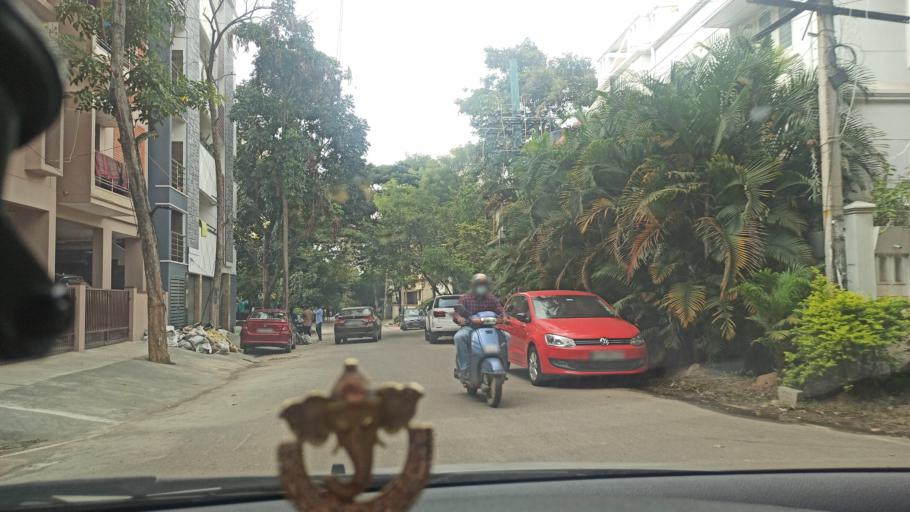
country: IN
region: Karnataka
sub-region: Bangalore Urban
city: Bangalore
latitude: 12.9172
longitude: 77.6470
